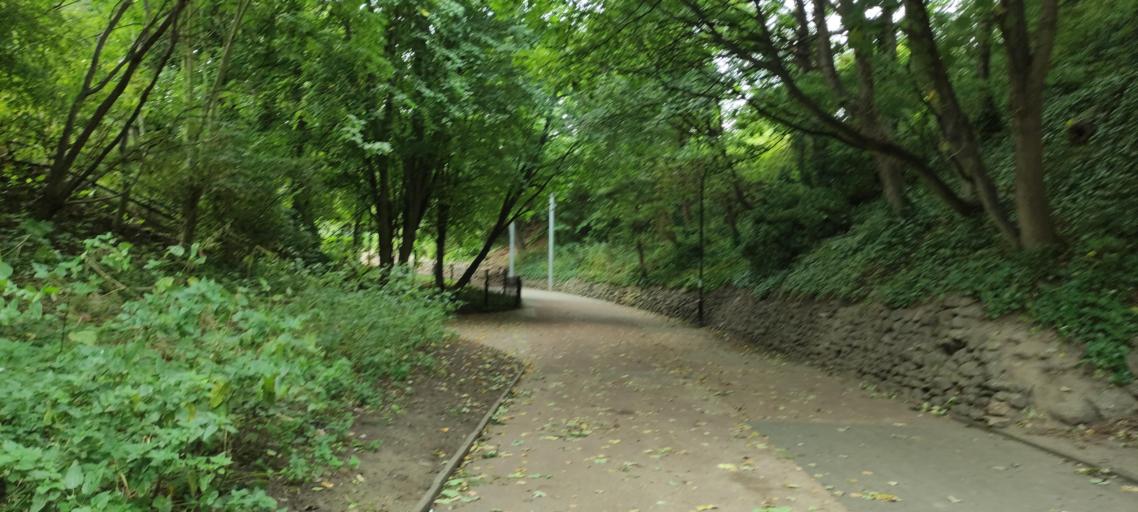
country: GB
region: England
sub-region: Sunderland
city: Sunderland
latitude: 54.9258
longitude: -1.3678
